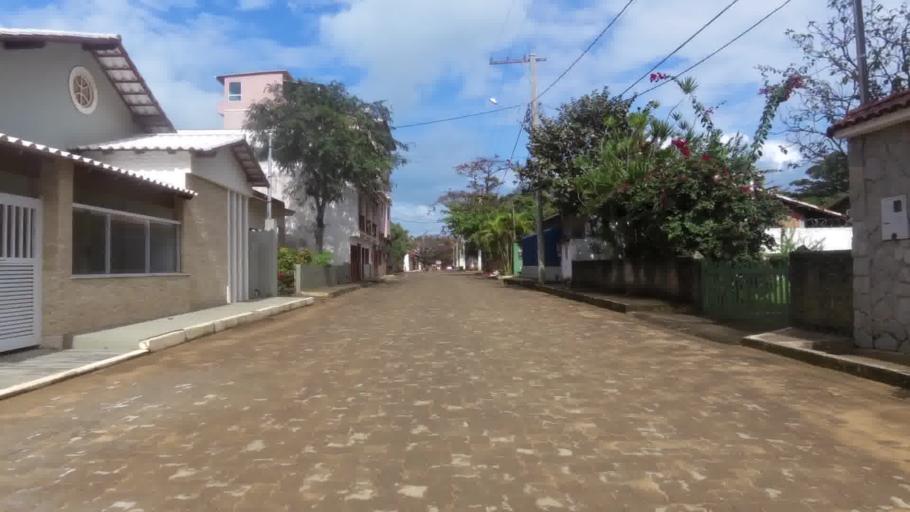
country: BR
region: Espirito Santo
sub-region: Piuma
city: Piuma
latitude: -20.8290
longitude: -40.6917
